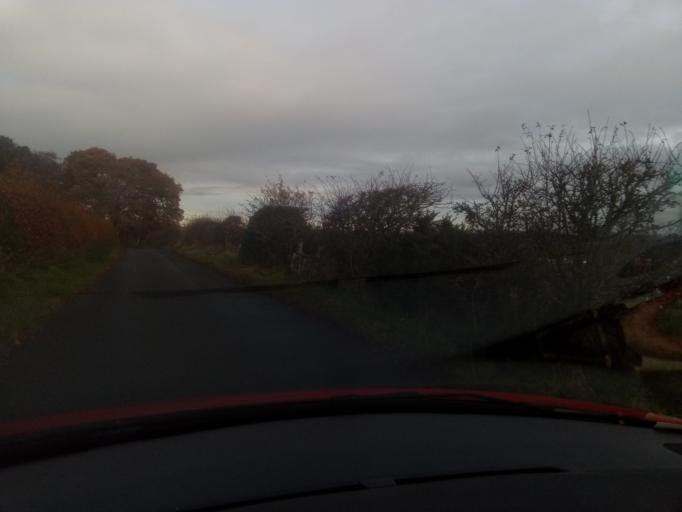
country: GB
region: Scotland
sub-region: The Scottish Borders
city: Jedburgh
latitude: 55.4783
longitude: -2.5674
